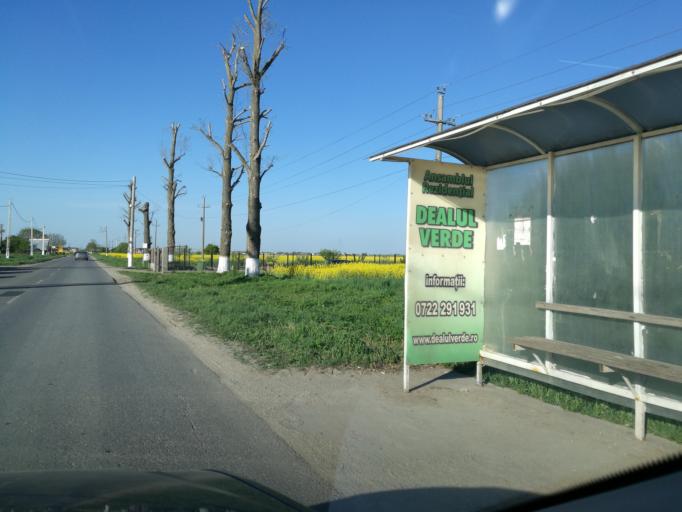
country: RO
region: Ilfov
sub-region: Comuna Vidra
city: Vidra
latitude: 44.2817
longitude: 26.1795
